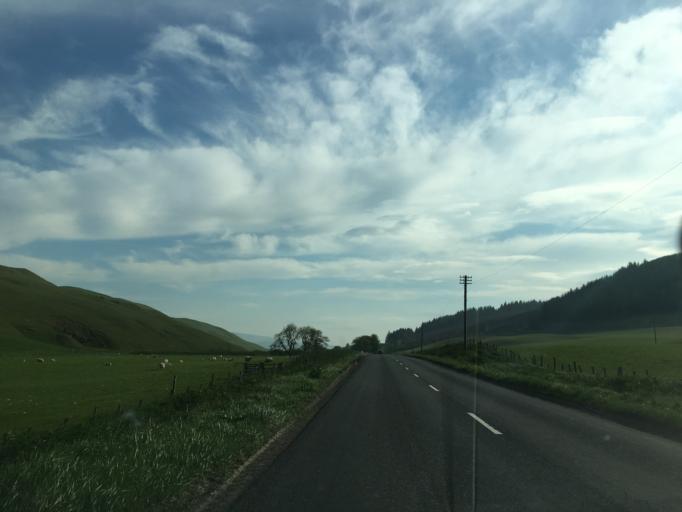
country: GB
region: Scotland
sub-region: The Scottish Borders
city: West Linton
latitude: 55.6684
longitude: -3.4210
